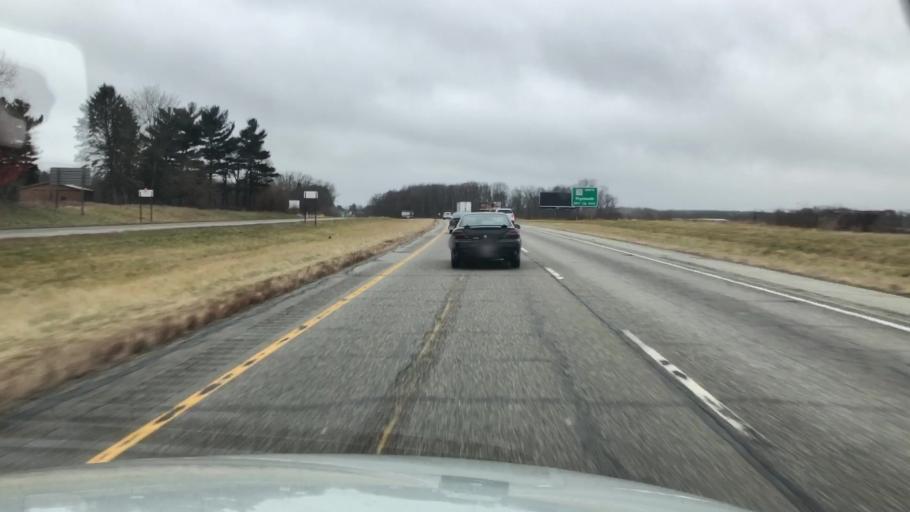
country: US
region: Indiana
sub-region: Marshall County
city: Plymouth
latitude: 41.3617
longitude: -86.2963
